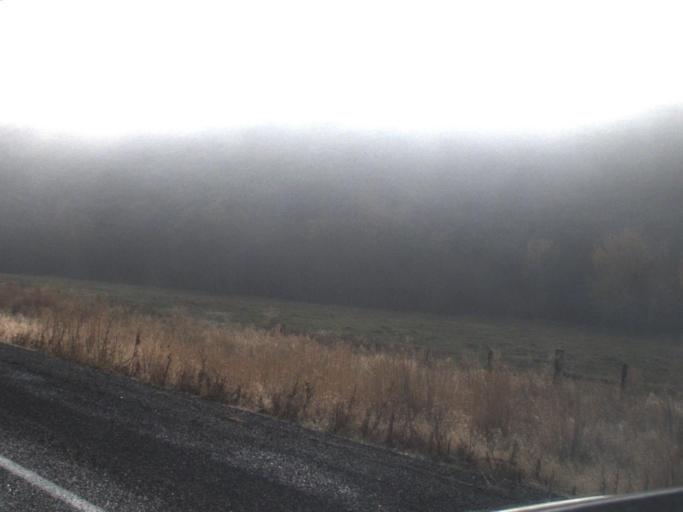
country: US
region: Washington
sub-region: Asotin County
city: Clarkston Heights-Vineland
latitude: 46.4265
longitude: -117.3001
